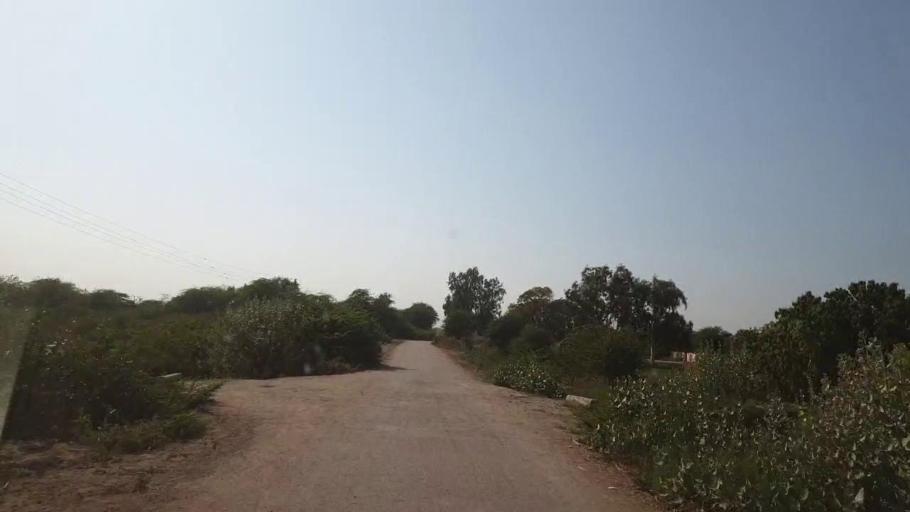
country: PK
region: Sindh
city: Nabisar
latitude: 25.0241
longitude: 69.4709
